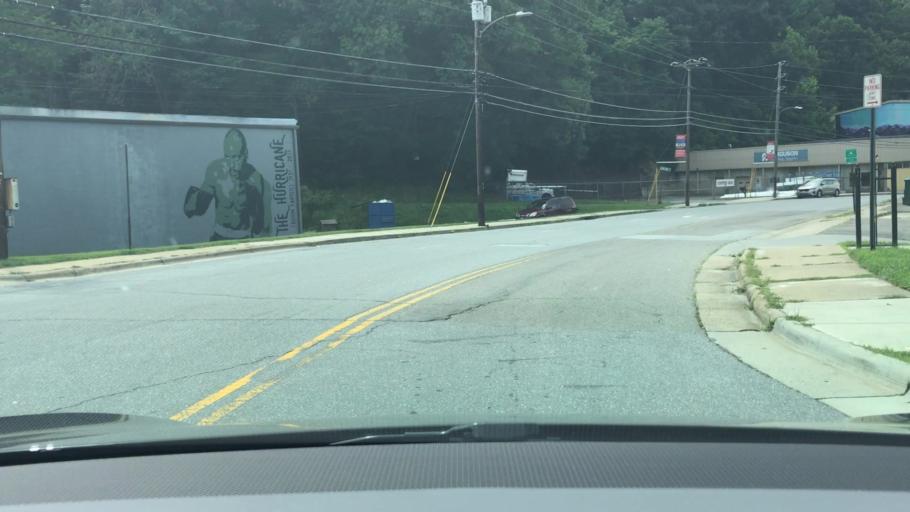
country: US
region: North Carolina
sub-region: Buncombe County
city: Asheville
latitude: 35.5874
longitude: -82.5643
